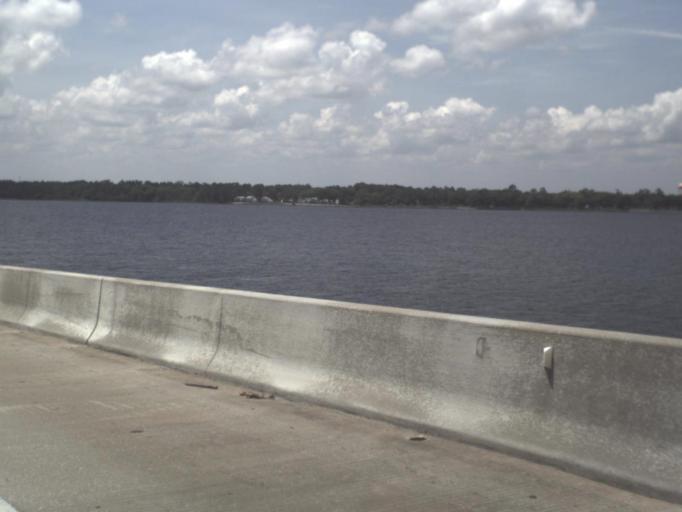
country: US
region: Florida
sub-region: Clay County
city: Orange Park
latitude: 30.1905
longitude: -81.6728
